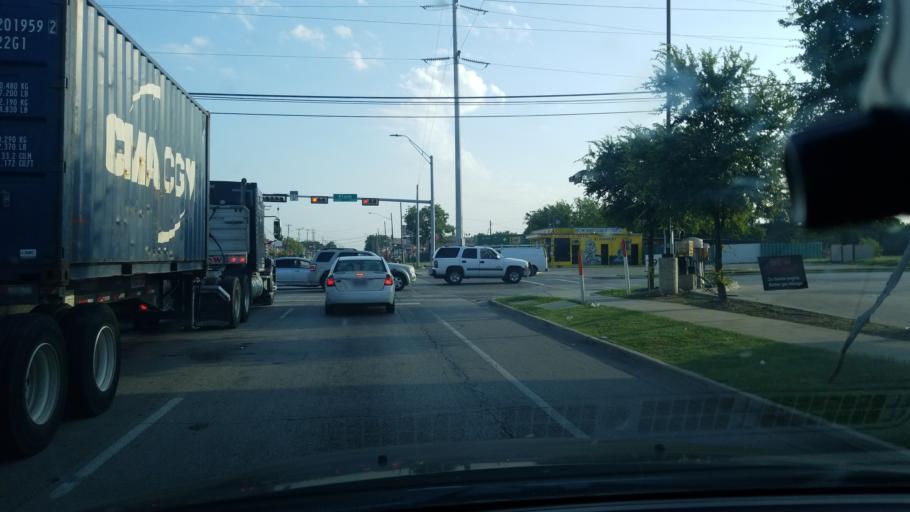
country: US
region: Texas
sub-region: Dallas County
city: Balch Springs
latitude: 32.7193
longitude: -96.6829
